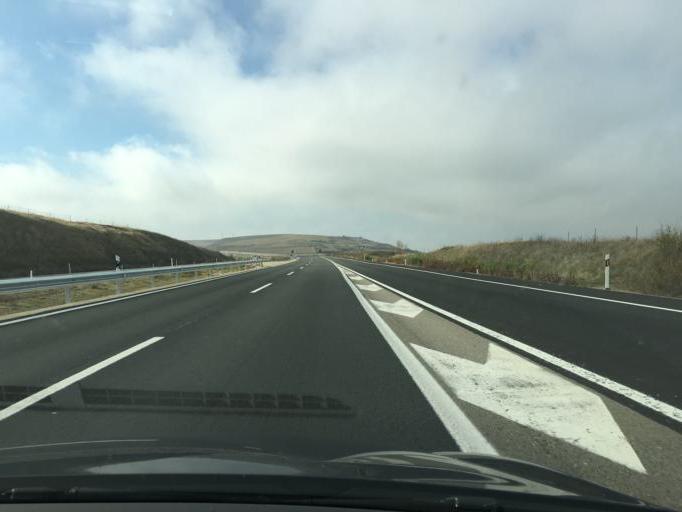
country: ES
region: Castille and Leon
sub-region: Provincia de Burgos
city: Villanueva de Teba
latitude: 42.6229
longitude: -3.1697
